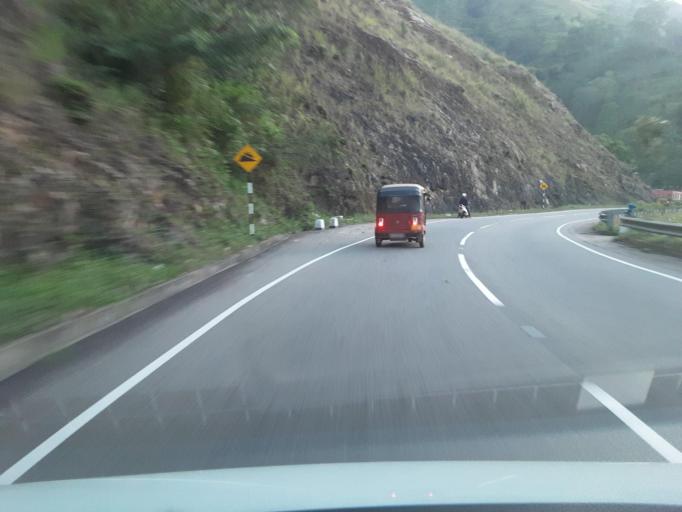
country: LK
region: Uva
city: Badulla
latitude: 6.9161
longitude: 80.9561
